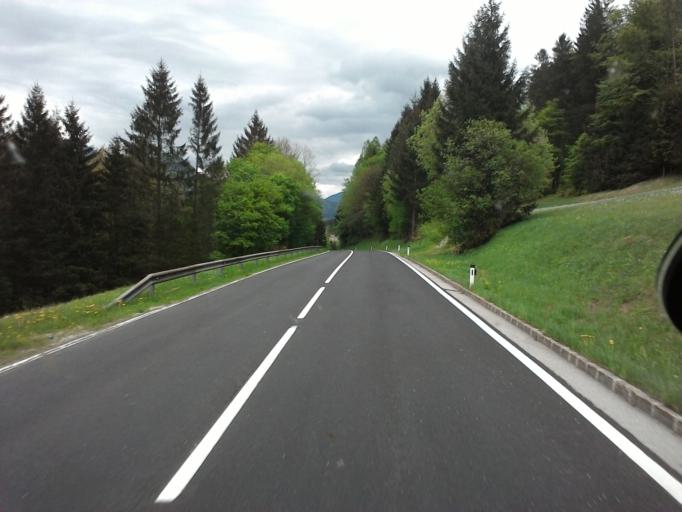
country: AT
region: Upper Austria
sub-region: Politischer Bezirk Kirchdorf an der Krems
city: Rossleithen
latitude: 47.7458
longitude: 14.2483
